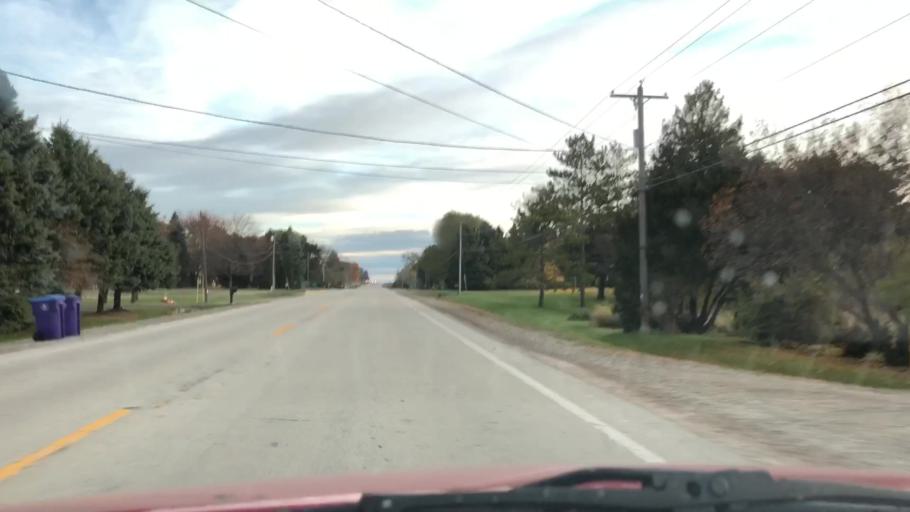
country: US
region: Wisconsin
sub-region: Brown County
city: Oneida
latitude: 44.4272
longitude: -88.2423
